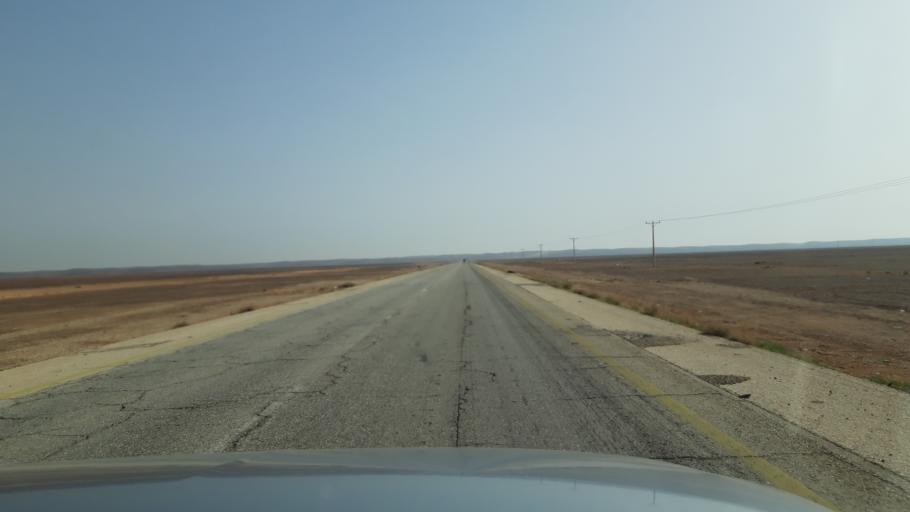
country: JO
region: Amman
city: Al Azraq ash Shamali
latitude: 31.8308
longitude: 36.6241
